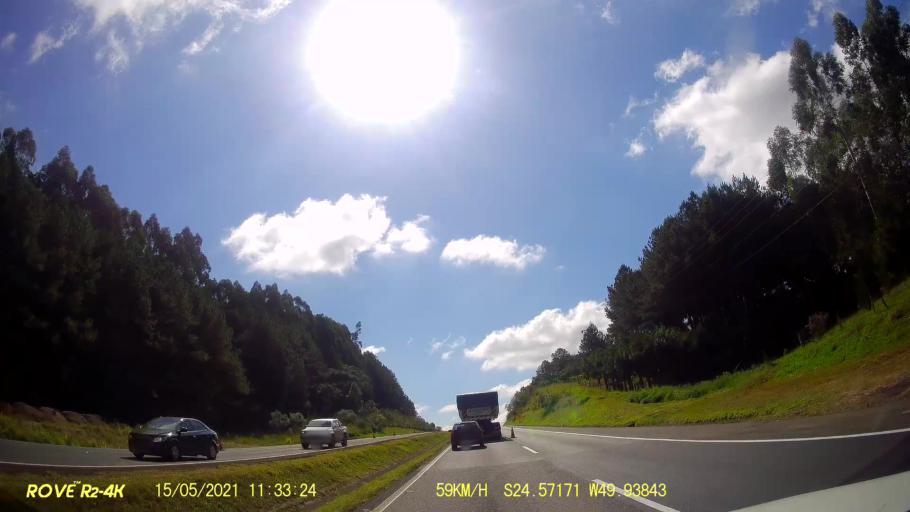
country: BR
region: Parana
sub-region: Pirai Do Sul
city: Pirai do Sul
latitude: -24.5718
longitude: -49.9385
